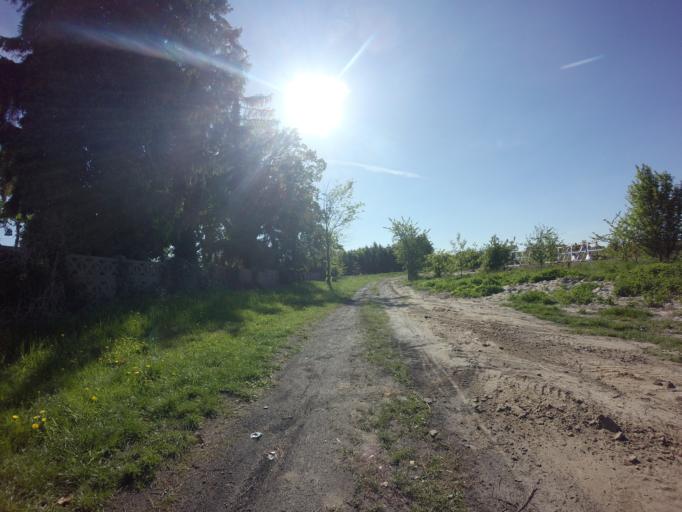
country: PL
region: West Pomeranian Voivodeship
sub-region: Powiat stargardzki
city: Dolice
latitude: 53.1616
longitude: 15.2846
